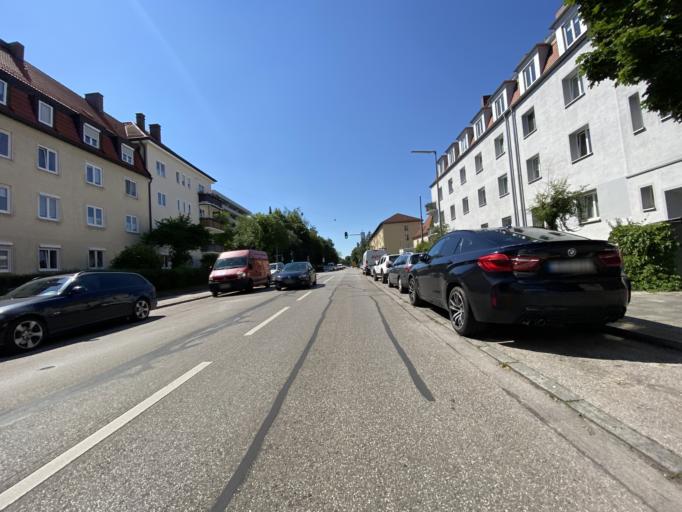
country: DE
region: Bavaria
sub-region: Upper Bavaria
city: Pullach im Isartal
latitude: 48.1132
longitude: 11.5260
